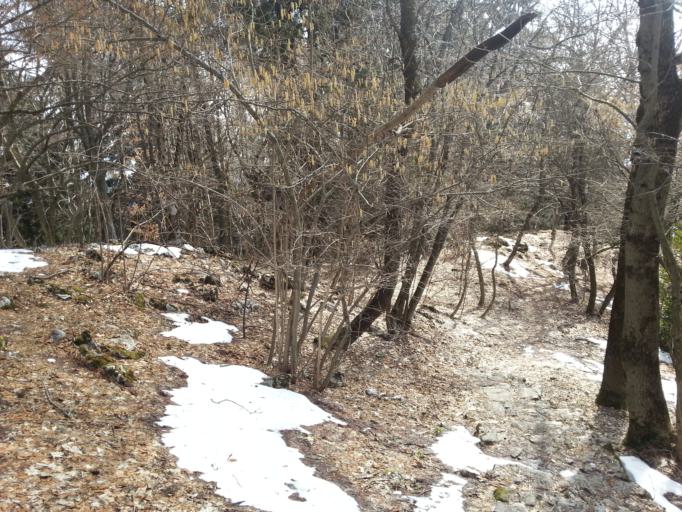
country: IT
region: Lombardy
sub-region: Provincia di Varese
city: Brinzio
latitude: 45.8675
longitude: 8.7734
